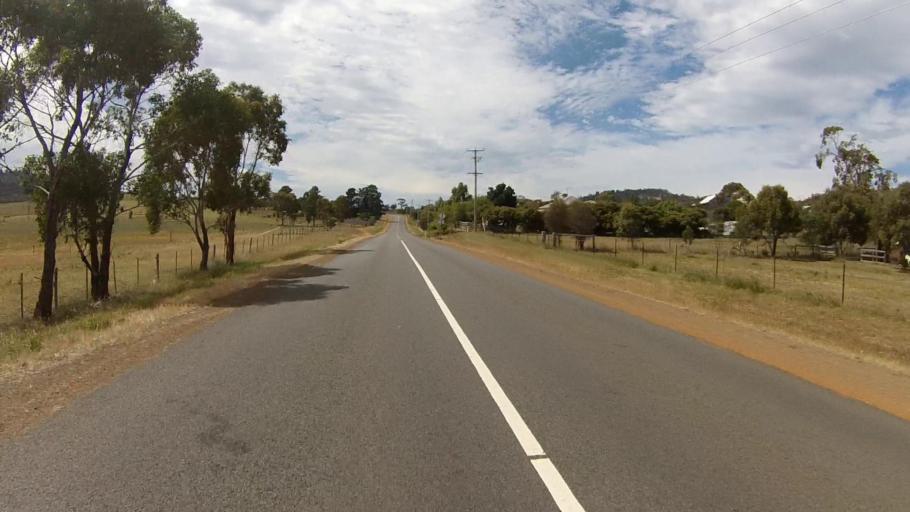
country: AU
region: Tasmania
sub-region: Brighton
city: Old Beach
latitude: -42.6932
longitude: 147.3468
